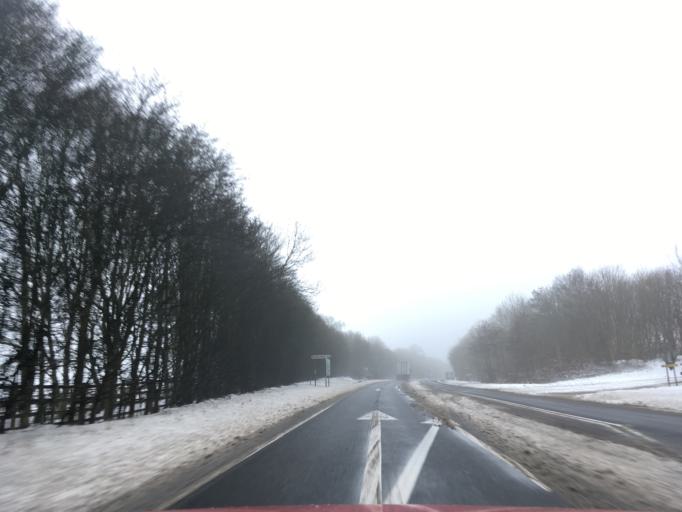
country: GB
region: England
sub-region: Warwickshire
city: Stratford-upon-Avon
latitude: 52.2286
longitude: -1.6978
